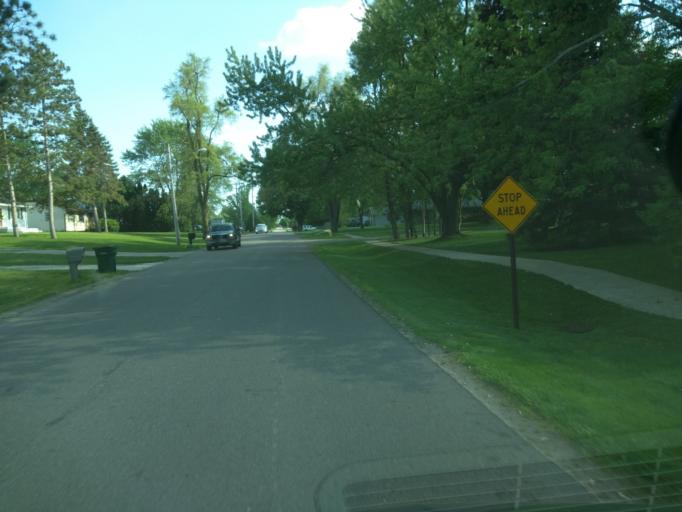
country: US
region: Michigan
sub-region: Eaton County
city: Waverly
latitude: 42.7355
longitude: -84.6054
